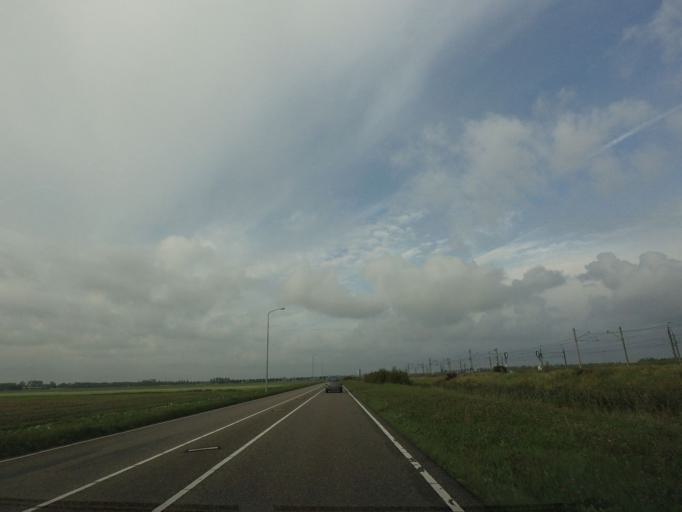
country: NL
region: North Holland
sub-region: Gemeente Haarlemmermeer
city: Hoofddorp
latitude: 52.2700
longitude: 4.6605
